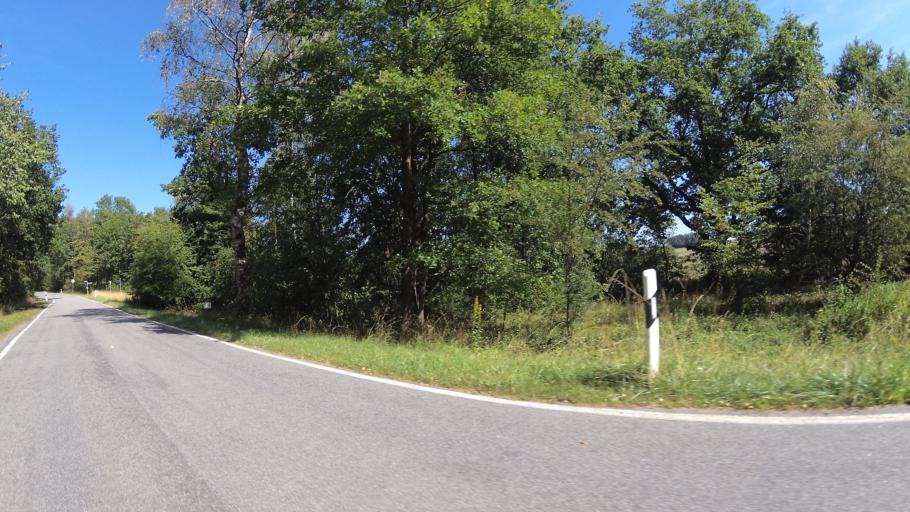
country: DE
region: Rheinland-Pfalz
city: Hornbach
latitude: 49.1468
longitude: 7.3156
